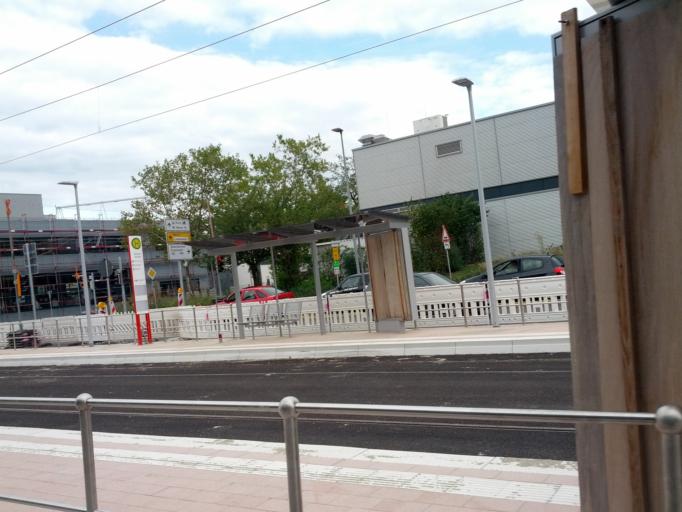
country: DE
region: Baden-Wuerttemberg
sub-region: Freiburg Region
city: Freiburg
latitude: 48.0097
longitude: 7.8314
